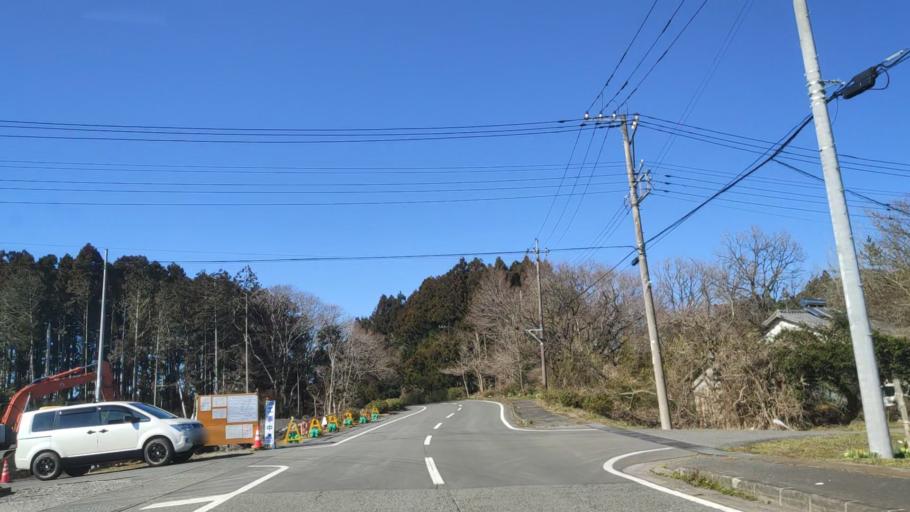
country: JP
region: Shizuoka
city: Fujinomiya
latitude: 35.3637
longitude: 138.6055
